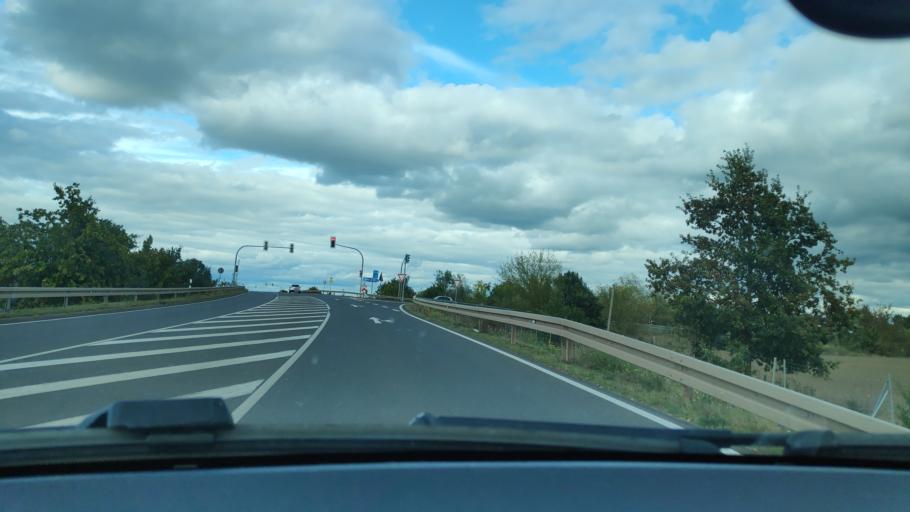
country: DE
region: Saxony-Anhalt
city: Schermen
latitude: 52.2240
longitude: 11.8210
